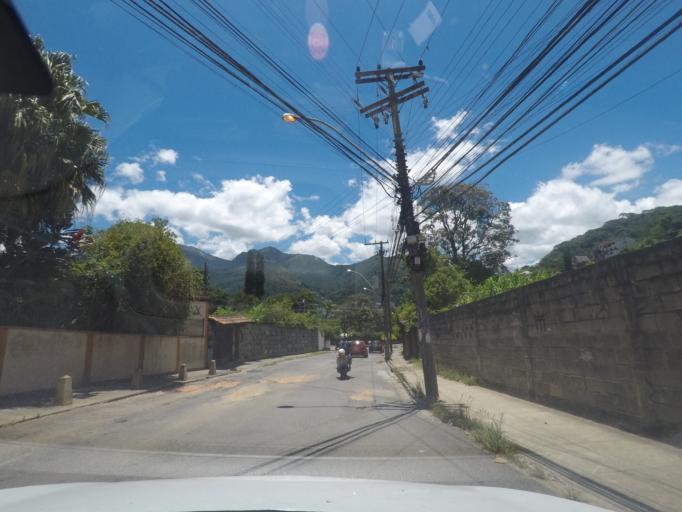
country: BR
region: Rio de Janeiro
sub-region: Teresopolis
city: Teresopolis
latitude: -22.4344
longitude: -42.9680
